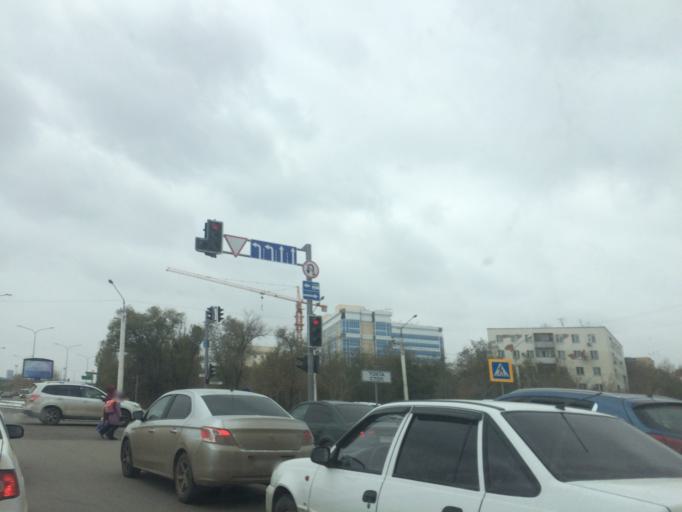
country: KZ
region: Astana Qalasy
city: Astana
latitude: 51.1615
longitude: 71.4684
